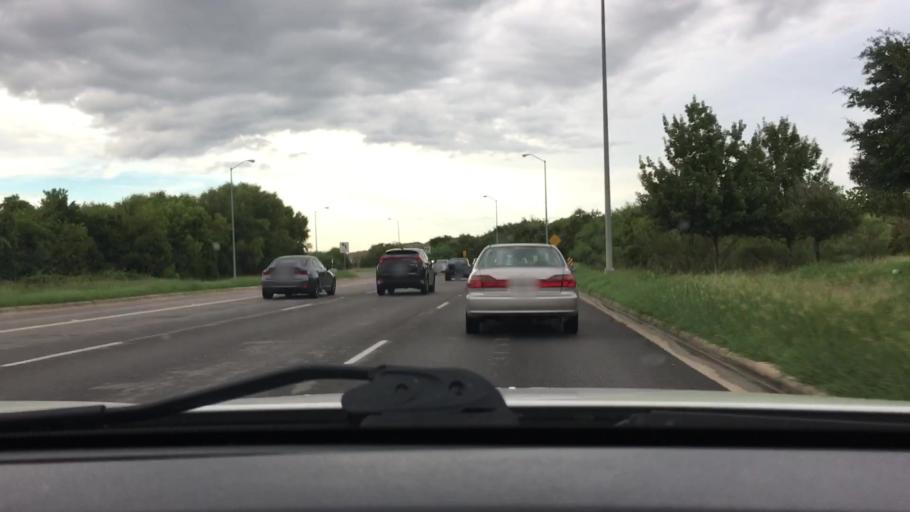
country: US
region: Texas
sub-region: Travis County
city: Windemere
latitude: 30.4883
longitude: -97.6506
